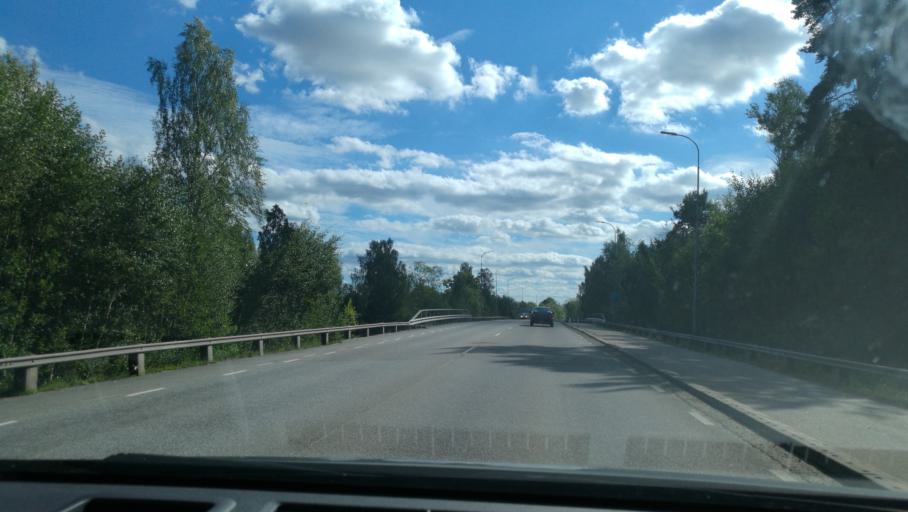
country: SE
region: Vaestra Goetaland
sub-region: Mariestads Kommun
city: Mariestad
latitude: 58.6912
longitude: 13.8172
